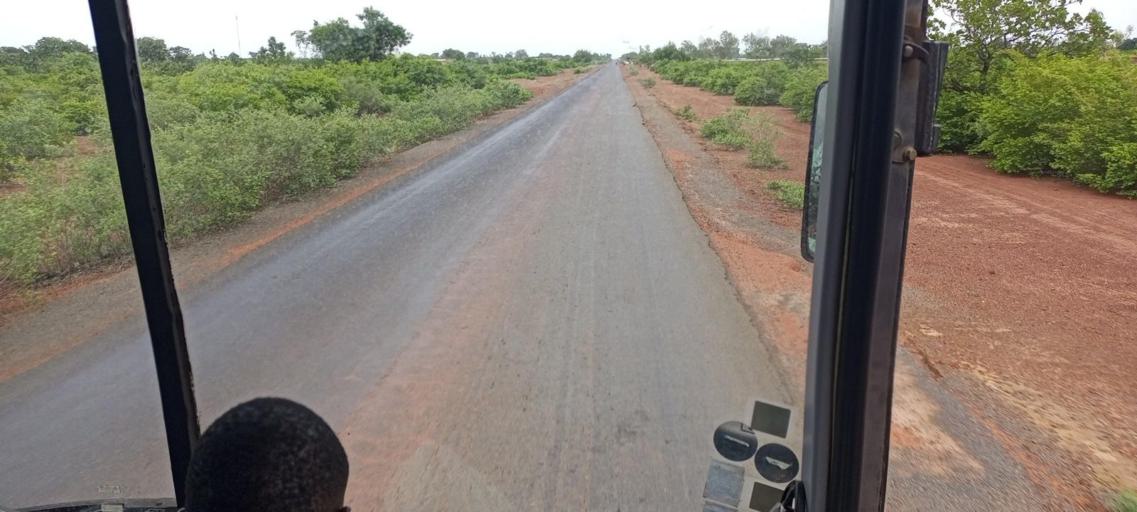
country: ML
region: Sikasso
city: Koutiala
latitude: 12.5421
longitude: -5.5767
